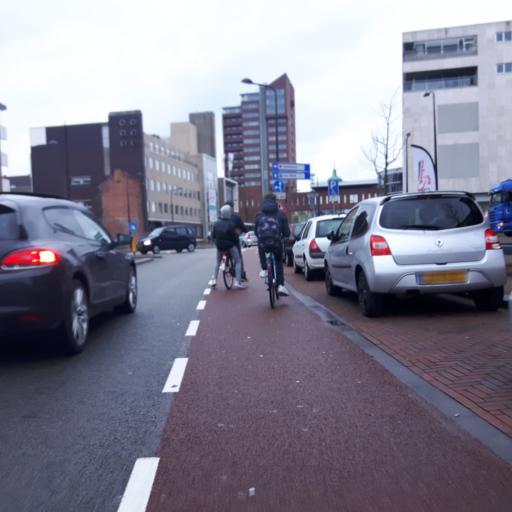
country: NL
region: Overijssel
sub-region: Gemeente Enschede
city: Enschede
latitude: 52.2161
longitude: 6.8961
